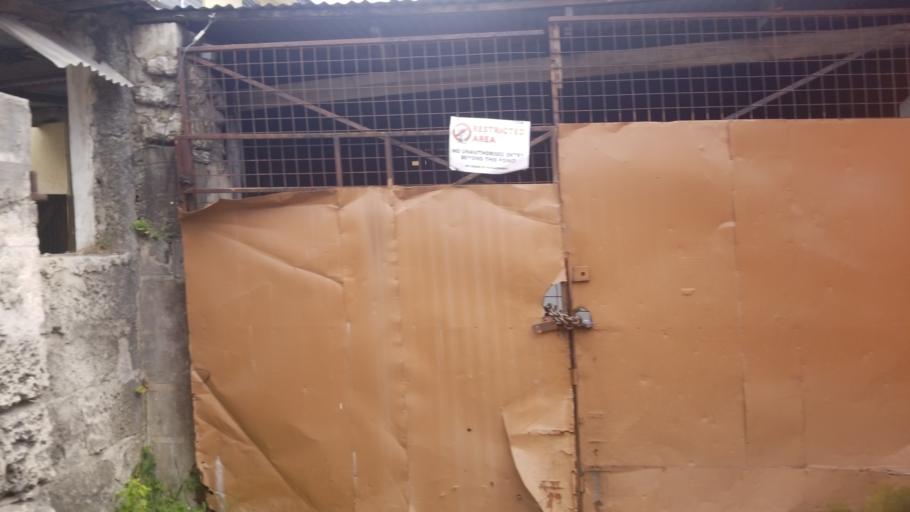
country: BB
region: Saint Michael
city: Bridgetown
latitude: 13.1013
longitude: -59.6184
